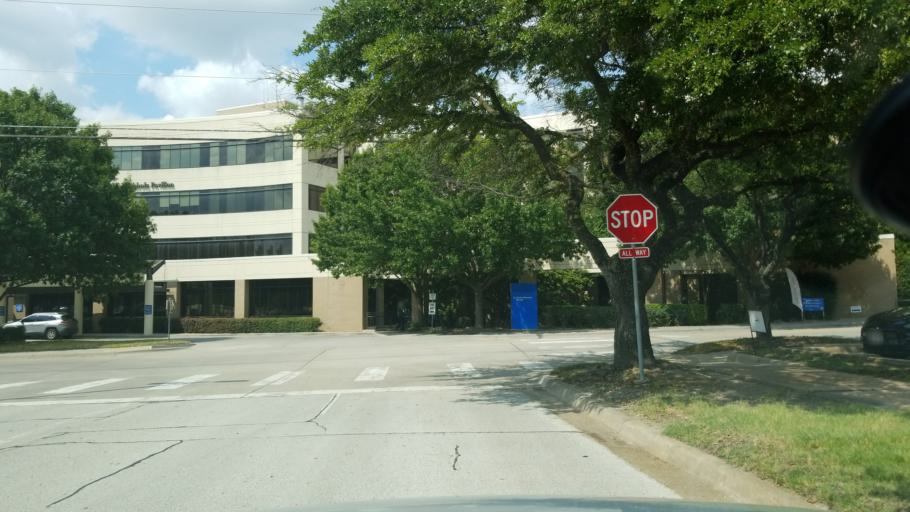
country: US
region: Texas
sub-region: Dallas County
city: Garland
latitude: 32.9184
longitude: -96.6619
